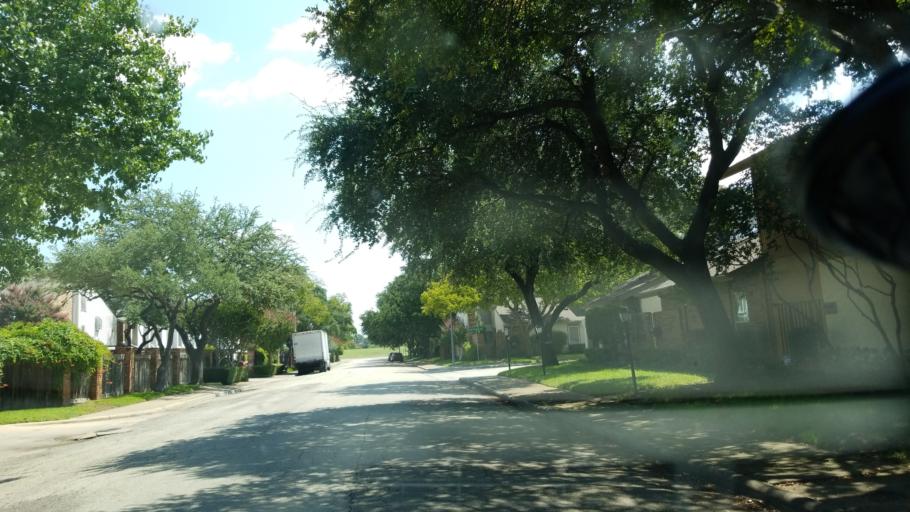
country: US
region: Texas
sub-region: Dallas County
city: Richardson
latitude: 32.9223
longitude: -96.7375
